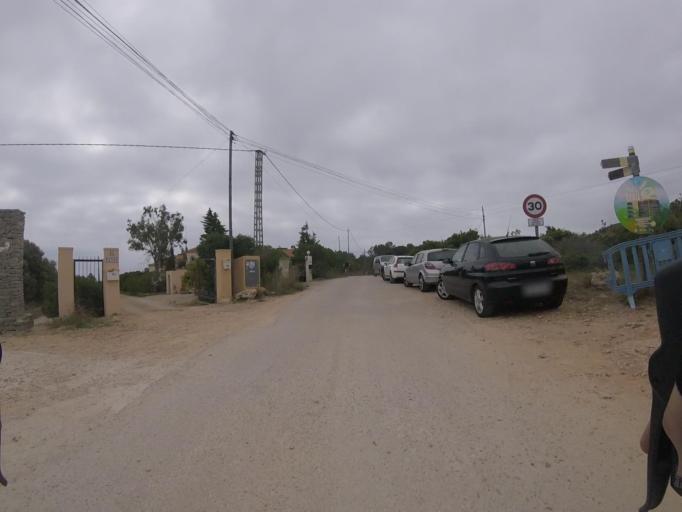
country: ES
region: Valencia
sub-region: Provincia de Castello
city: Peniscola
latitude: 40.3357
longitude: 0.3738
